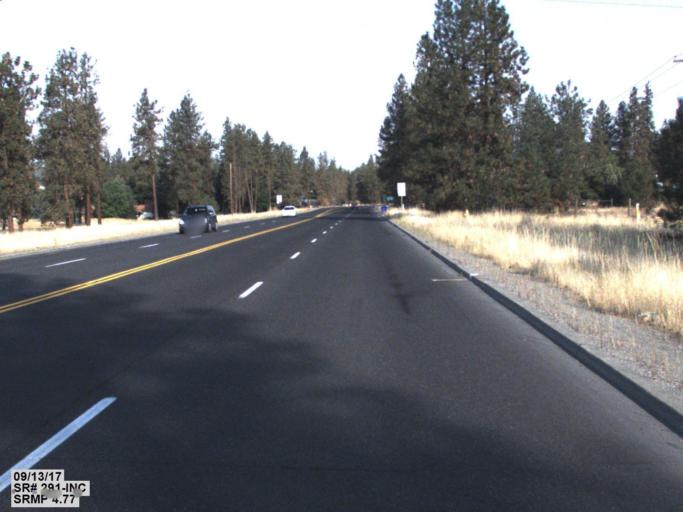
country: US
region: Washington
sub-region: Spokane County
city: Town and Country
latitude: 47.7316
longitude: -117.5033
